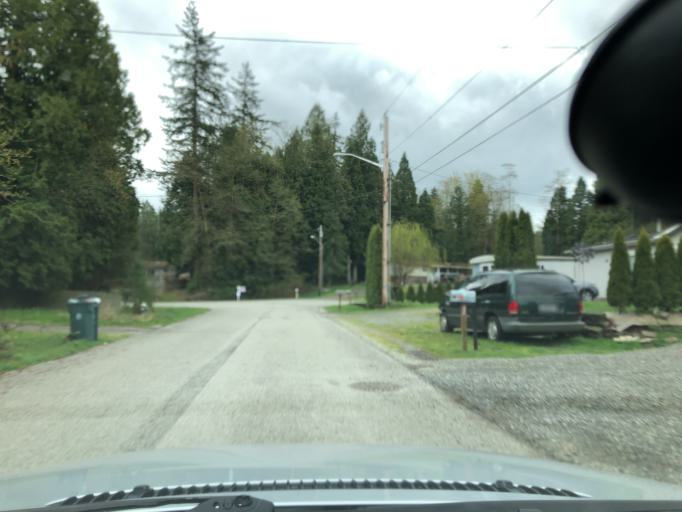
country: US
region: Washington
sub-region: Whatcom County
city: Birch Bay
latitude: 48.9550
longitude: -122.7337
